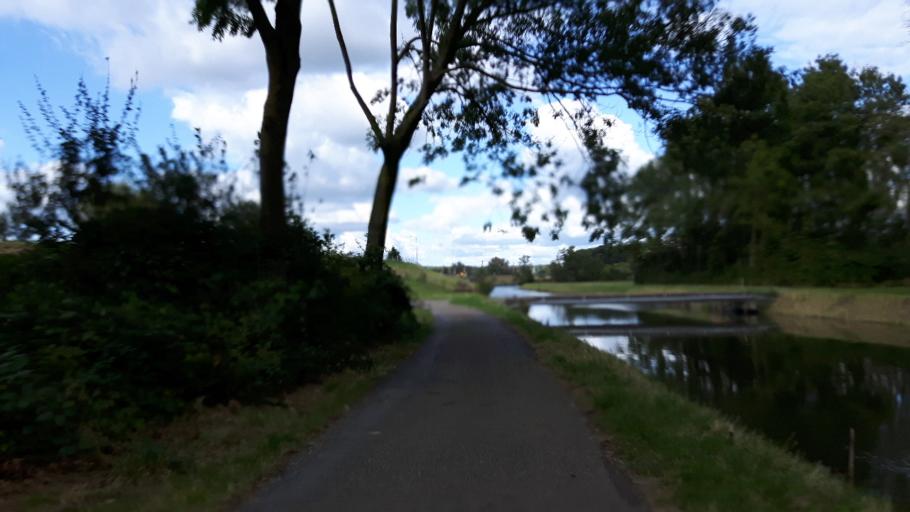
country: NL
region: South Holland
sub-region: Gemeente Leerdam
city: Leerdam
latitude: 51.8913
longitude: 5.1175
